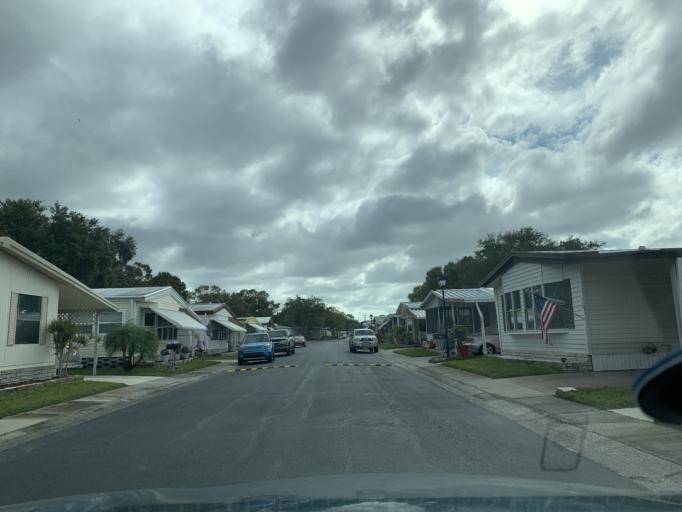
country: US
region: Florida
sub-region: Pinellas County
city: Ridgecrest
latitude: 27.8829
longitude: -82.7924
